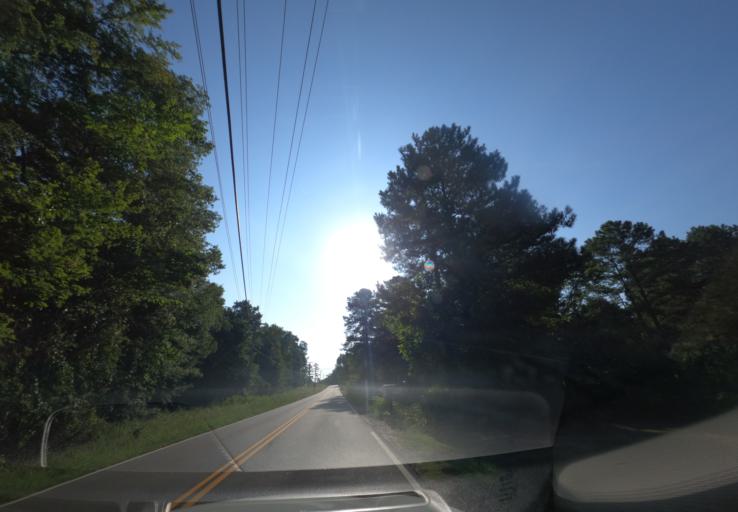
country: US
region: South Carolina
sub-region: Edgefield County
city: Murphys Estates
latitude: 33.5830
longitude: -81.9856
